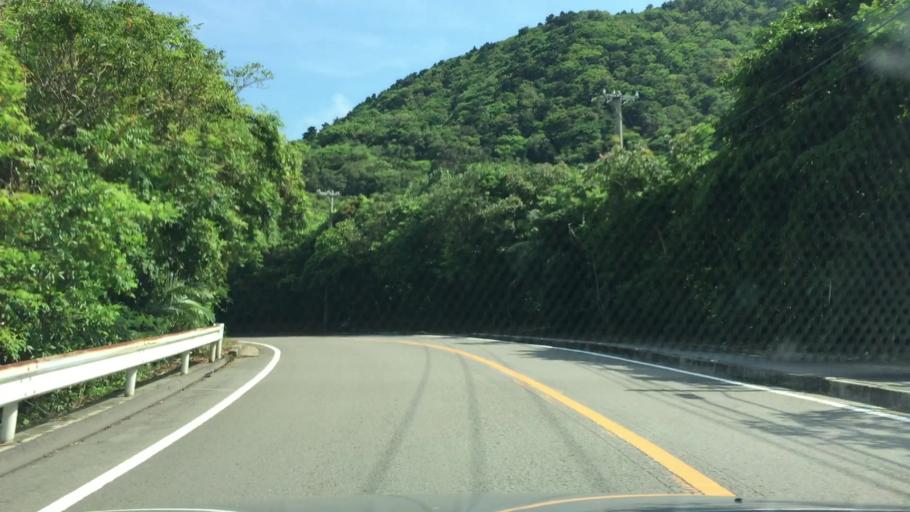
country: JP
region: Okinawa
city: Ishigaki
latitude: 24.5131
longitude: 124.2653
